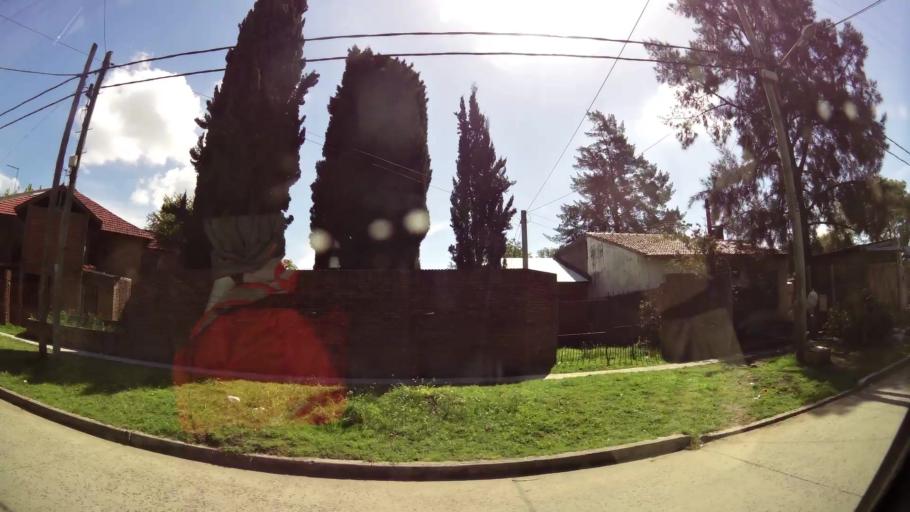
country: AR
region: Buenos Aires
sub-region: Partido de Quilmes
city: Quilmes
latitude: -34.8007
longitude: -58.2699
